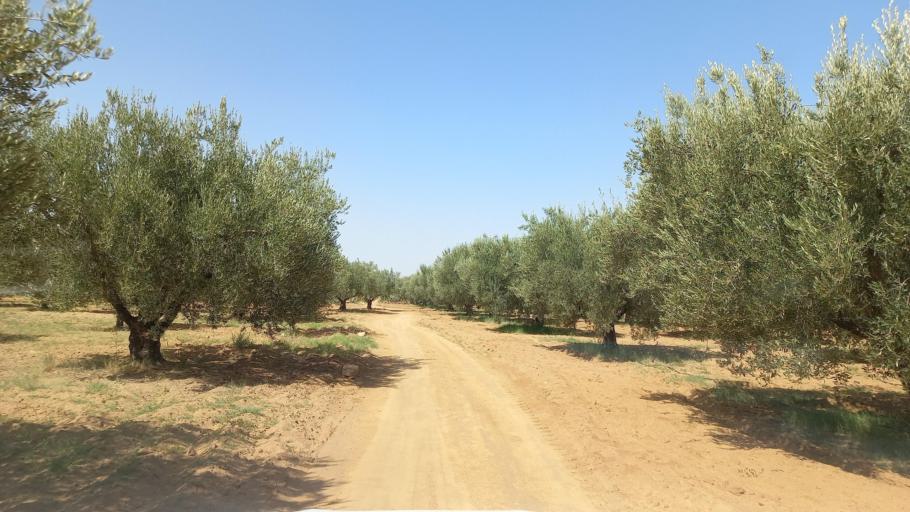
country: TN
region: Al Qasrayn
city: Kasserine
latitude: 35.2222
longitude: 9.0429
